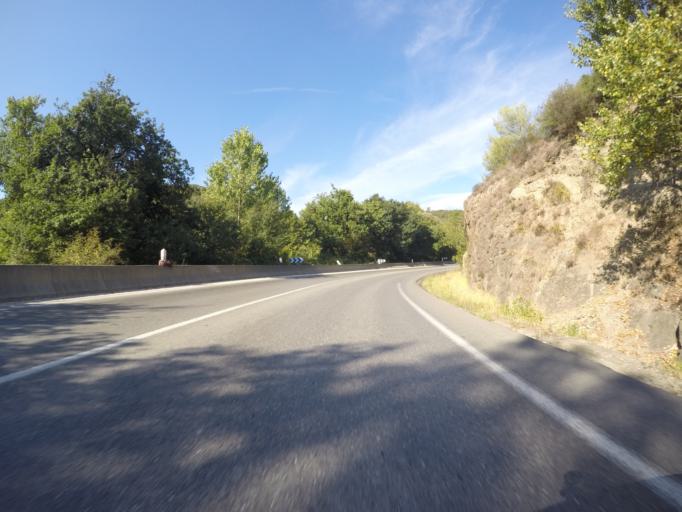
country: FR
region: Provence-Alpes-Cote d'Azur
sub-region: Departement des Alpes-Maritimes
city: Villeneuve-Loubet
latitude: 43.6568
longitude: 7.1072
